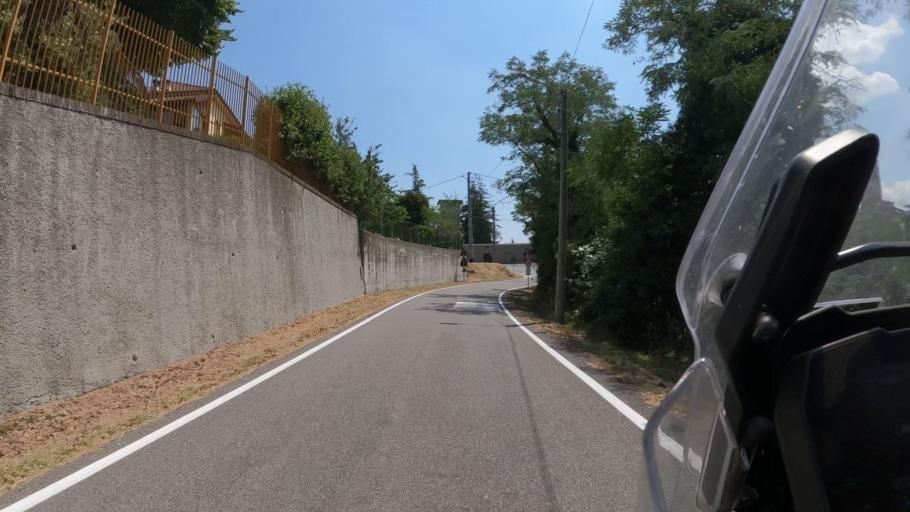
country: IT
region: Piedmont
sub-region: Provincia di Alessandria
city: Cassinelle-Concentrico
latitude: 44.5780
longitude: 8.5535
